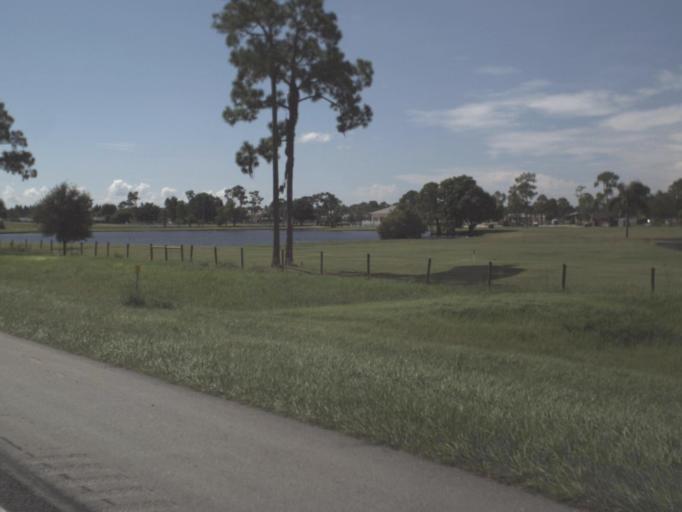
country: US
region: Florida
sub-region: Charlotte County
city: Charlotte Park
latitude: 26.8882
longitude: -81.9952
